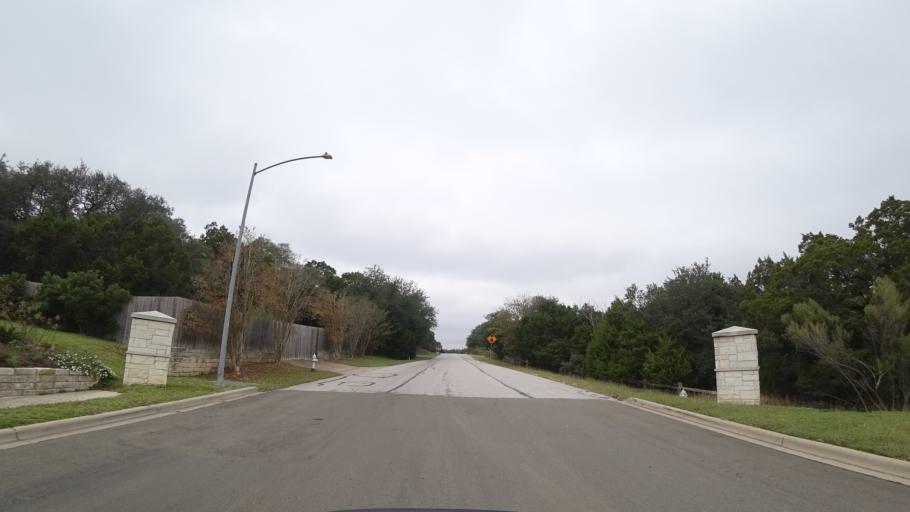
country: US
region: Texas
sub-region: Travis County
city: Barton Creek
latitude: 30.2406
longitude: -97.9060
